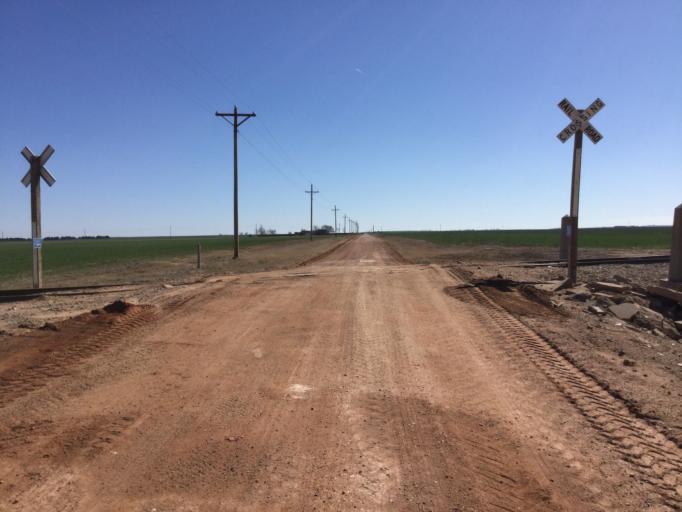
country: US
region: Kansas
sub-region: Barber County
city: Kiowa
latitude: 36.9986
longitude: -98.4832
